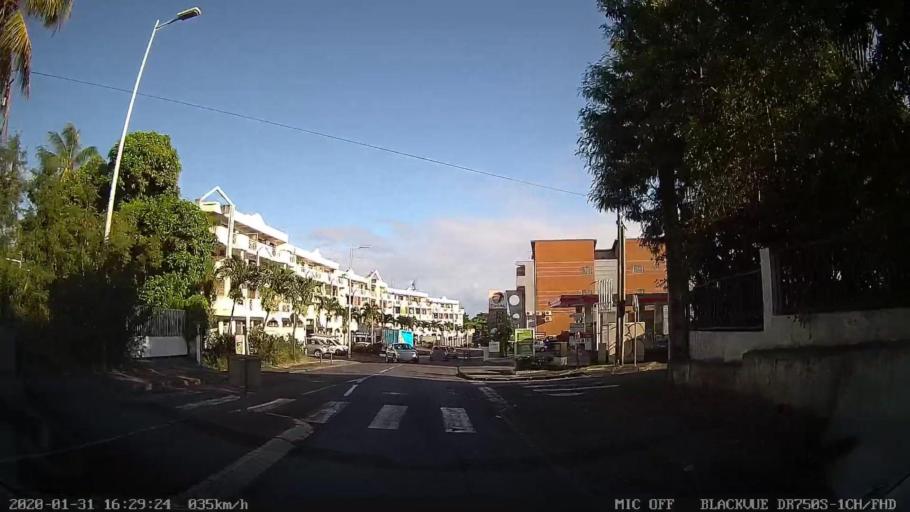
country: RE
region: Reunion
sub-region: Reunion
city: Saint-Denis
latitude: -20.8983
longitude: 55.4916
